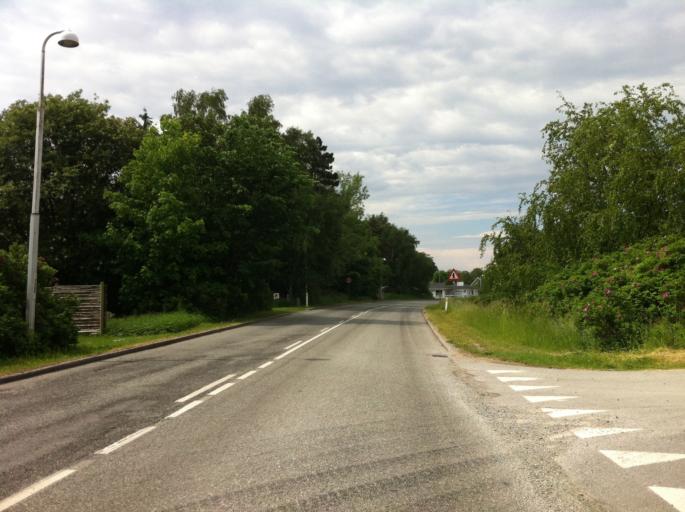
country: DK
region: Capital Region
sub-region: Gribskov Kommune
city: Helsinge
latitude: 56.1082
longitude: 12.1949
